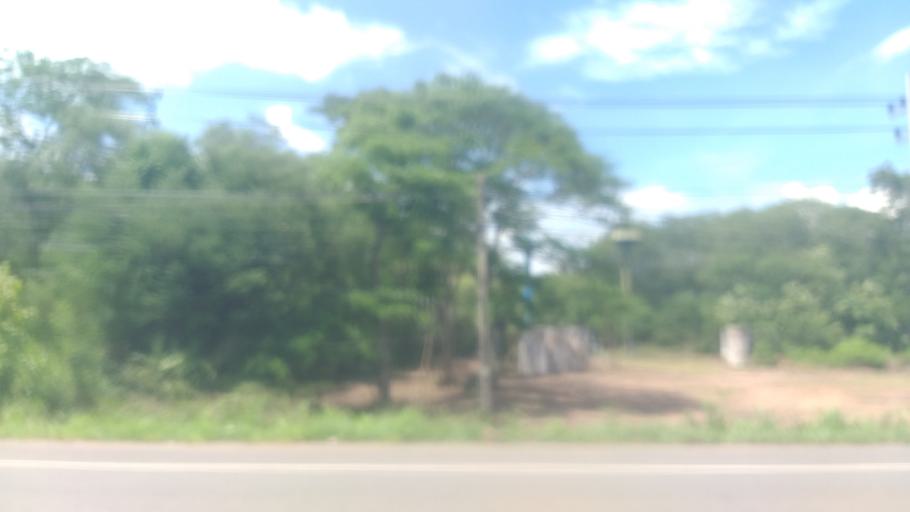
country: TH
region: Nakhon Ratchasima
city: Phra Thong Kham
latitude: 15.2941
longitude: 101.9884
